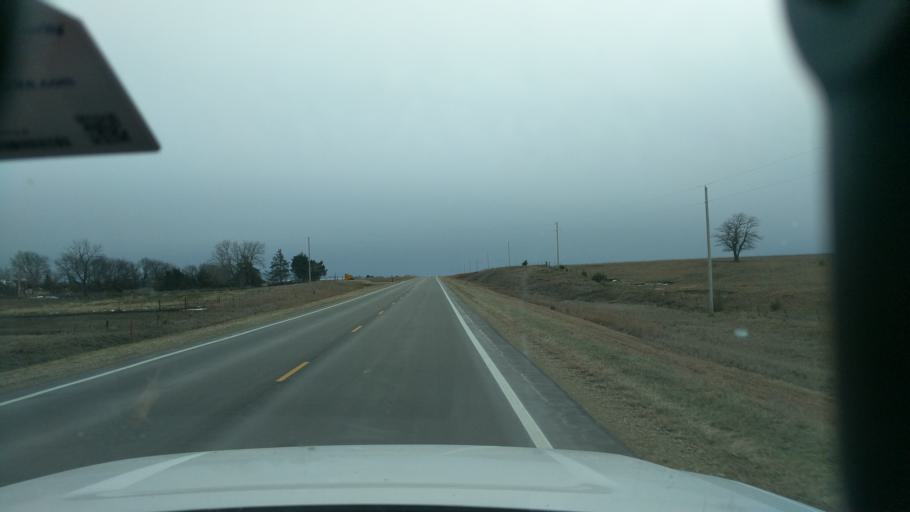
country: US
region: Kansas
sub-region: Dickinson County
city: Herington
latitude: 38.7534
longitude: -96.9275
